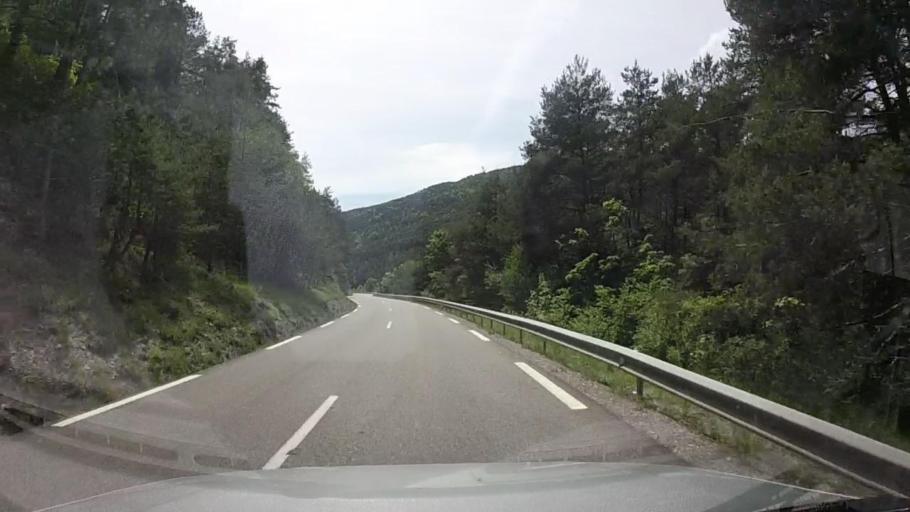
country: FR
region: Provence-Alpes-Cote d'Azur
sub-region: Departement des Alpes-de-Haute-Provence
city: Le Brusquet
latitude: 44.2238
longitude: 6.3612
